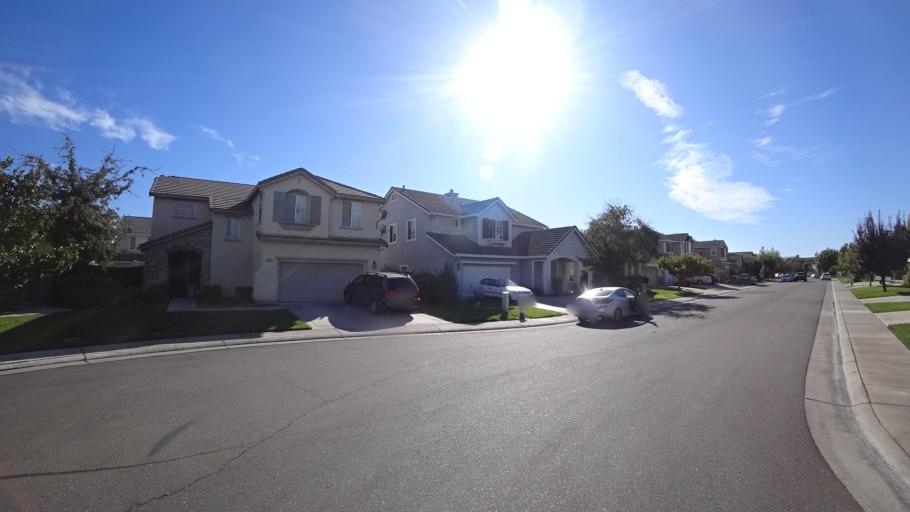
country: US
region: California
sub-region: Sacramento County
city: Laguna
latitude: 38.4130
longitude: -121.4824
